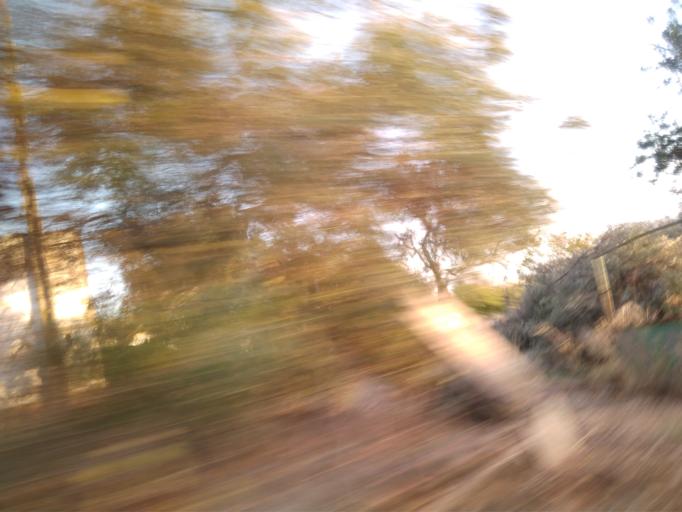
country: PT
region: Faro
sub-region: Faro
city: Santa Barbara de Nexe
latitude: 37.0808
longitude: -7.9588
